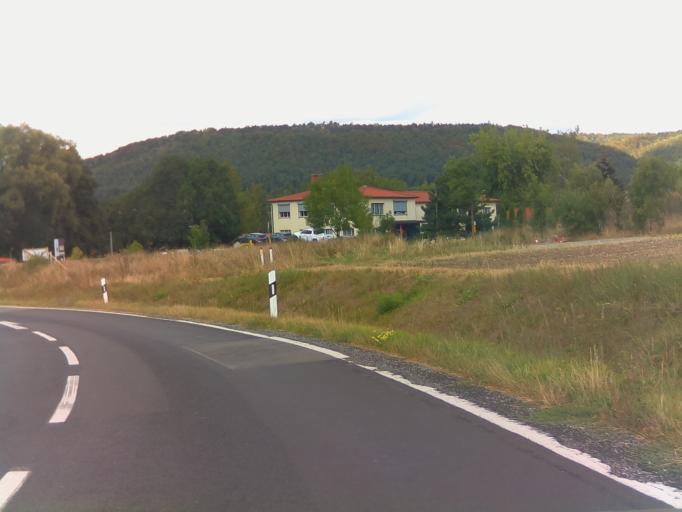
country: DE
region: Thuringia
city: Ritschenhausen
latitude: 50.5200
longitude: 10.4337
